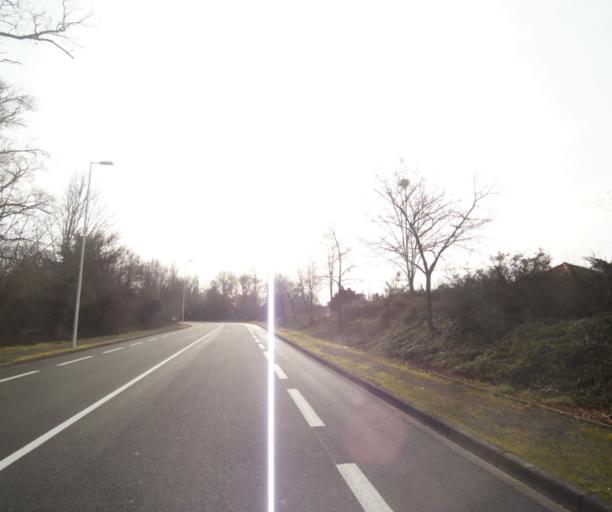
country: FR
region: Rhone-Alpes
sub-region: Departement de la Loire
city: Riorges
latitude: 46.0294
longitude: 4.0473
